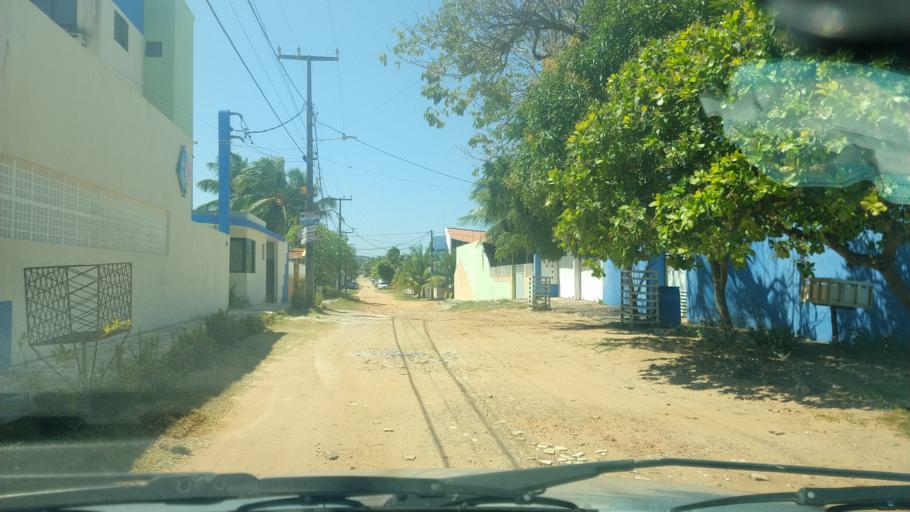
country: BR
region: Rio Grande do Norte
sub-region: Parnamirim
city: Parnamirim
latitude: -5.9563
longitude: -35.1516
